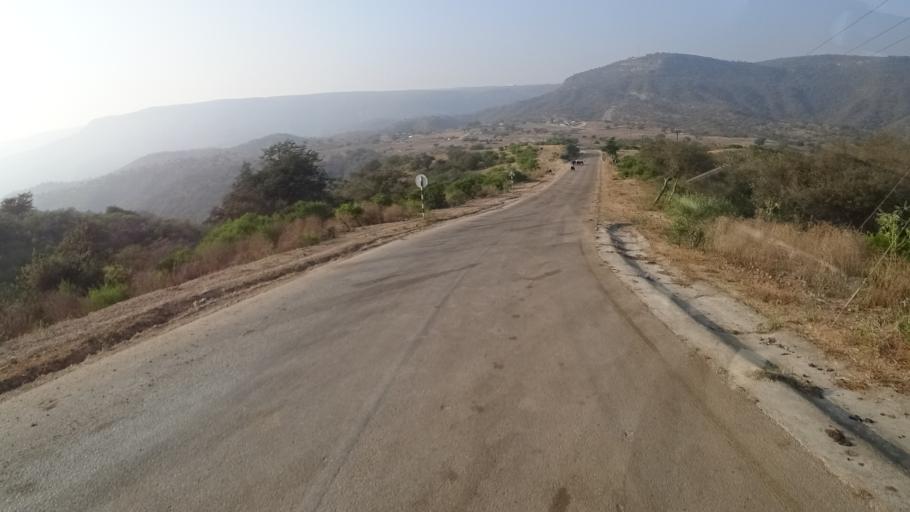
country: YE
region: Al Mahrah
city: Hawf
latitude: 16.7469
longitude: 53.3443
